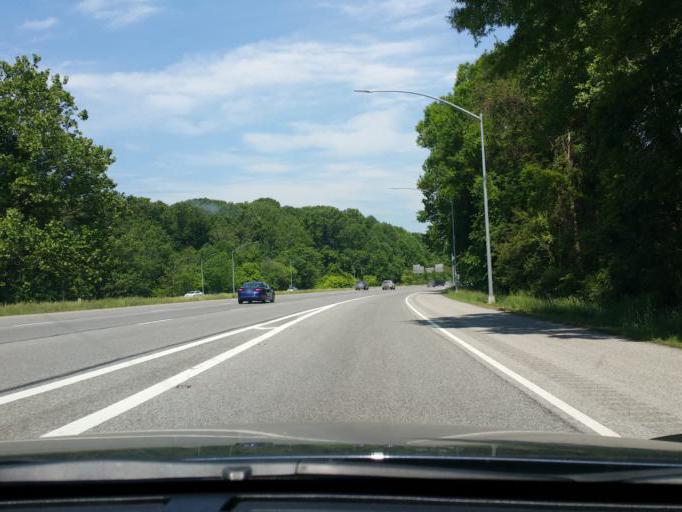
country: US
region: Maryland
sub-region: Howard County
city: Savage
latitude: 39.1611
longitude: -76.8311
